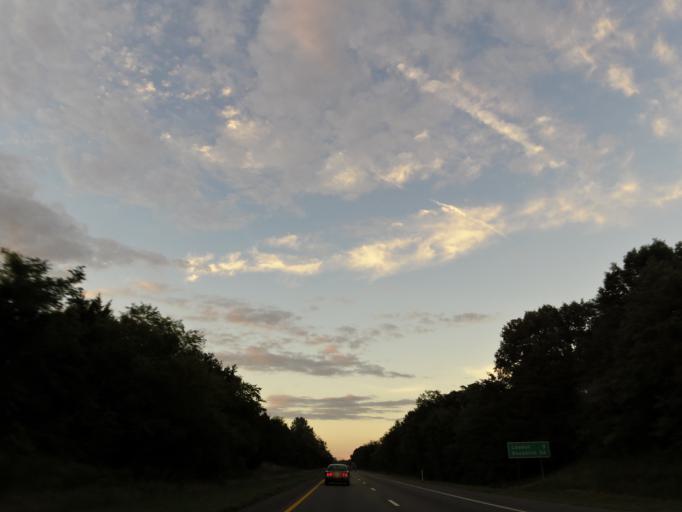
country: US
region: Tennessee
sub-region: Loudon County
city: Loudon
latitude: 35.7071
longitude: -84.4203
